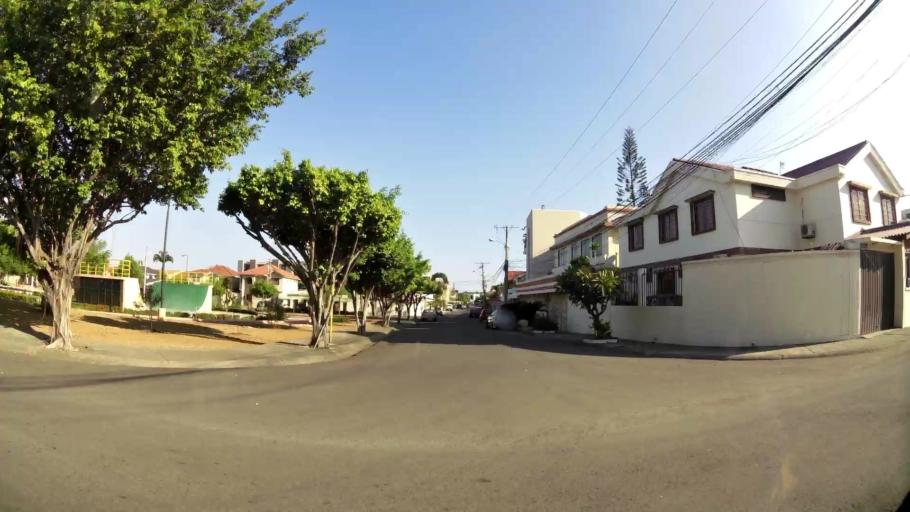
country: EC
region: Guayas
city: Santa Lucia
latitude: -2.1867
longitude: -79.9702
